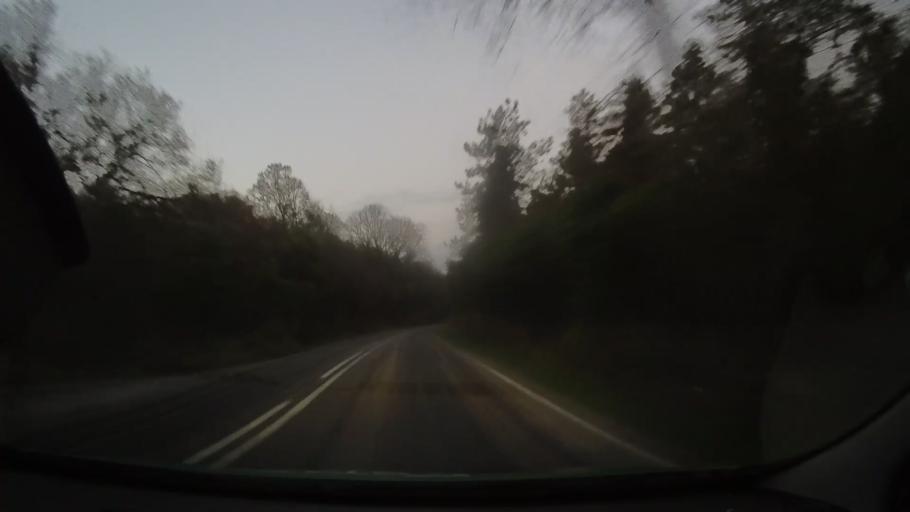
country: RO
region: Constanta
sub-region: Comuna Baneasa
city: Baneasa
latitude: 44.0803
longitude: 27.7391
